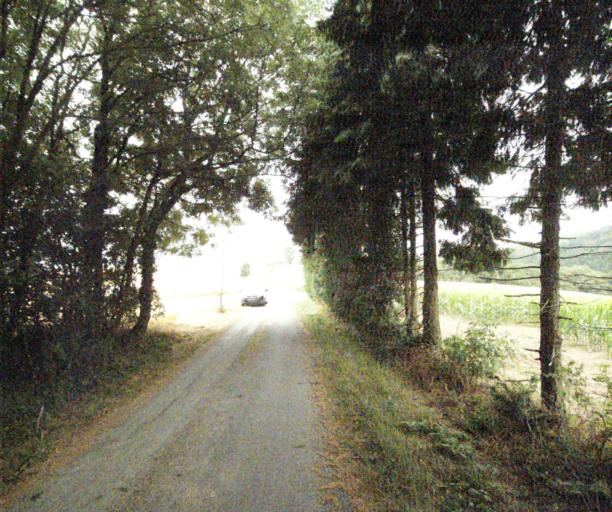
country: FR
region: Midi-Pyrenees
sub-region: Departement du Tarn
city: Soreze
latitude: 43.4014
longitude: 2.0447
